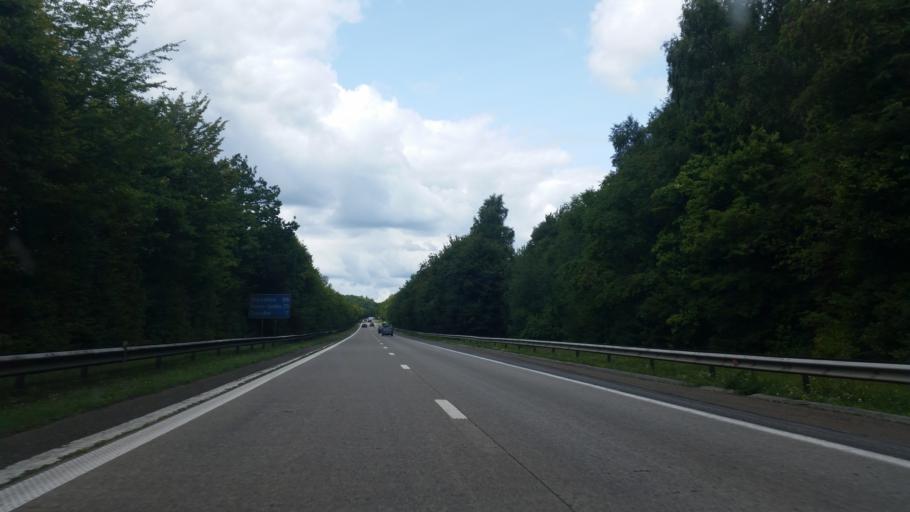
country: BE
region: Wallonia
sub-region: Province de Namur
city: Ciney
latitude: 50.2749
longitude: 5.0285
